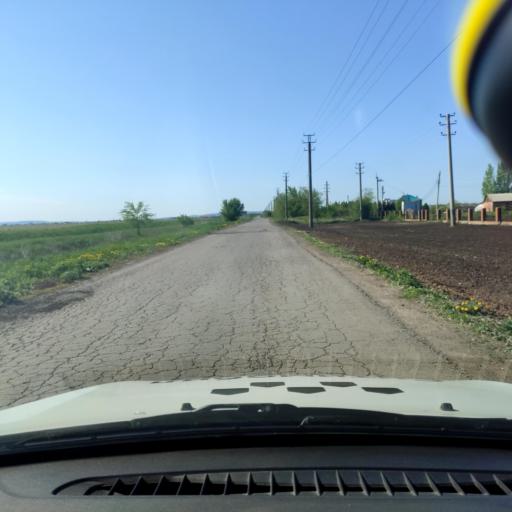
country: RU
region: Samara
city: Podstepki
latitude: 53.5373
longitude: 49.1997
